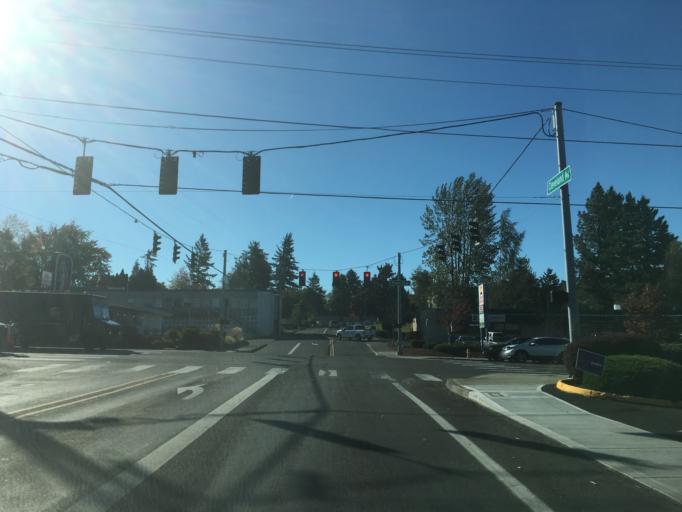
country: US
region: Oregon
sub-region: Multnomah County
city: Gresham
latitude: 45.4985
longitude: -122.4211
